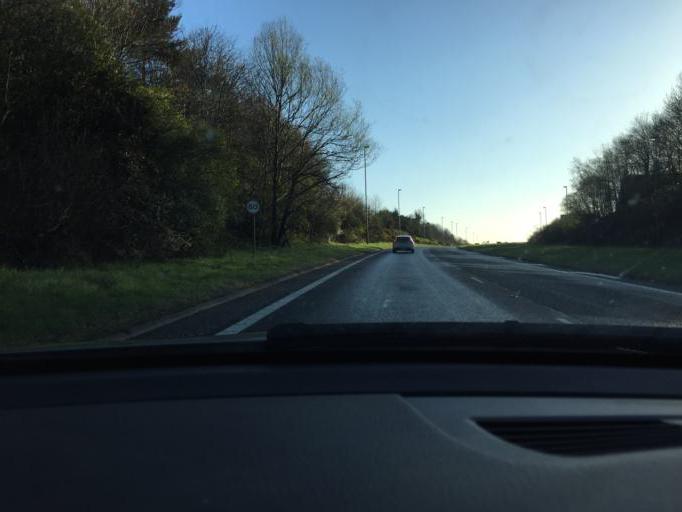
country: GB
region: Northern Ireland
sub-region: Banbridge District
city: Banbridge
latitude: 54.3450
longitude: -6.2527
